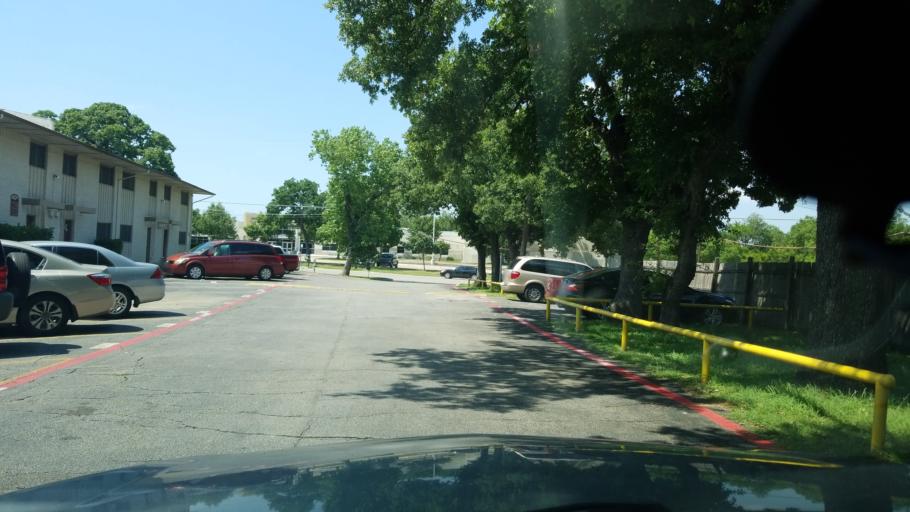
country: US
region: Texas
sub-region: Dallas County
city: Irving
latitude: 32.8181
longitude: -96.9543
